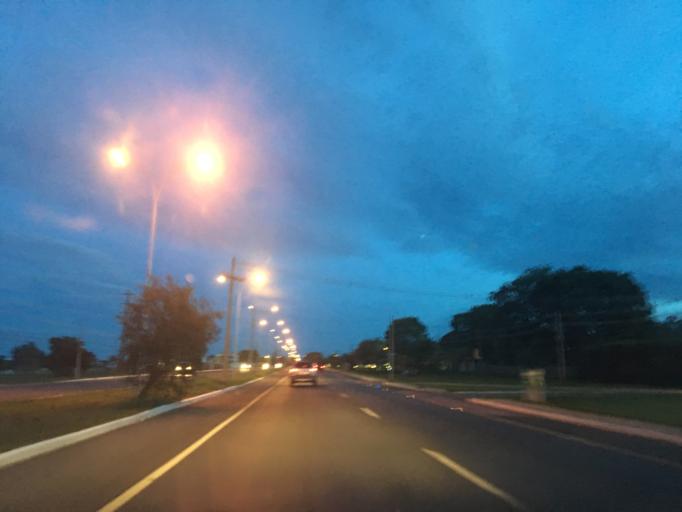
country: BR
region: Federal District
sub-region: Brasilia
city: Brasilia
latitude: -15.8538
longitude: -47.8427
